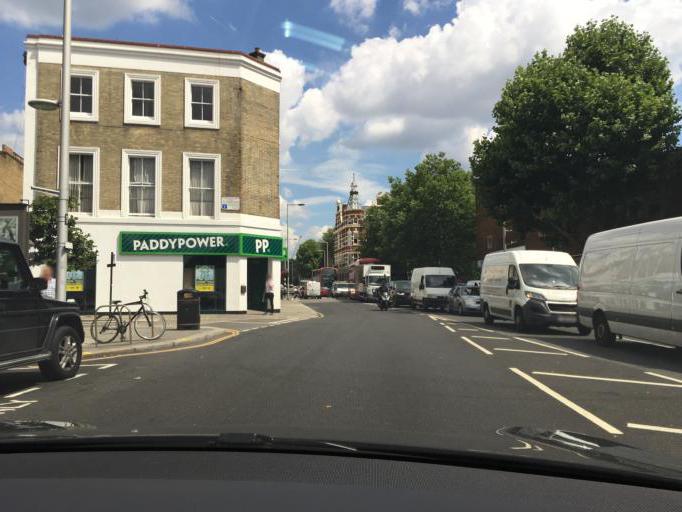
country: GB
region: England
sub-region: Greater London
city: Chelsea
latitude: 51.4817
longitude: -0.1813
